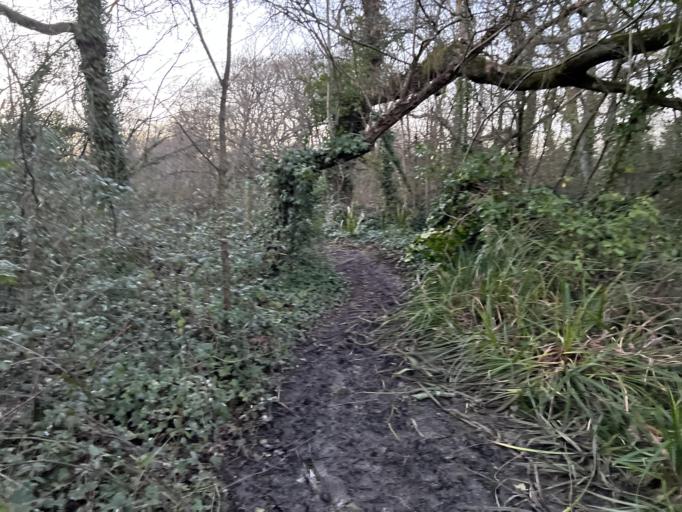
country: GB
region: England
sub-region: Isle of Wight
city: Newport
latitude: 50.7219
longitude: -1.2917
